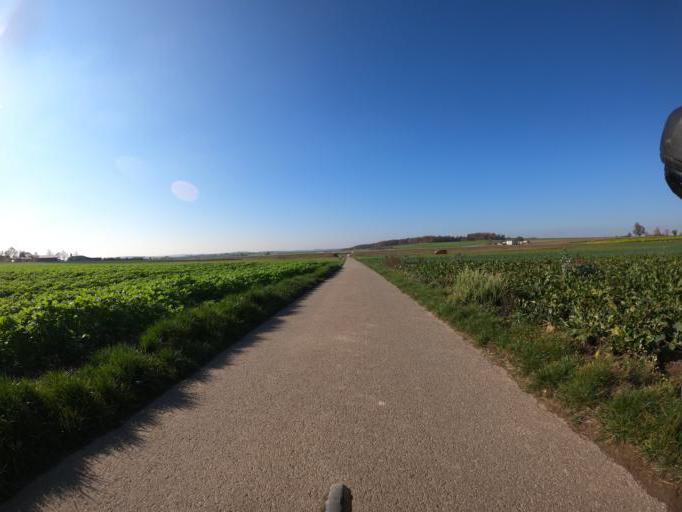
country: DE
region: Baden-Wuerttemberg
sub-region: Regierungsbezirk Stuttgart
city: Magstadt
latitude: 48.7265
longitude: 8.9509
